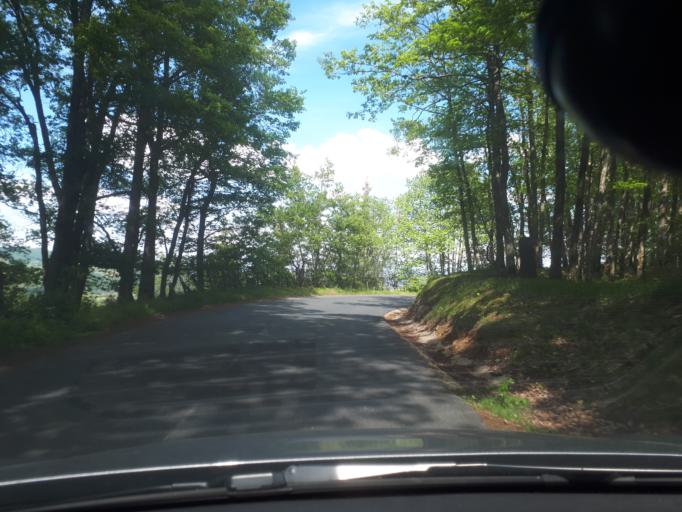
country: FR
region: Rhone-Alpes
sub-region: Departement du Rhone
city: Saint-Martin-en-Haut
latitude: 45.6550
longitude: 4.5741
